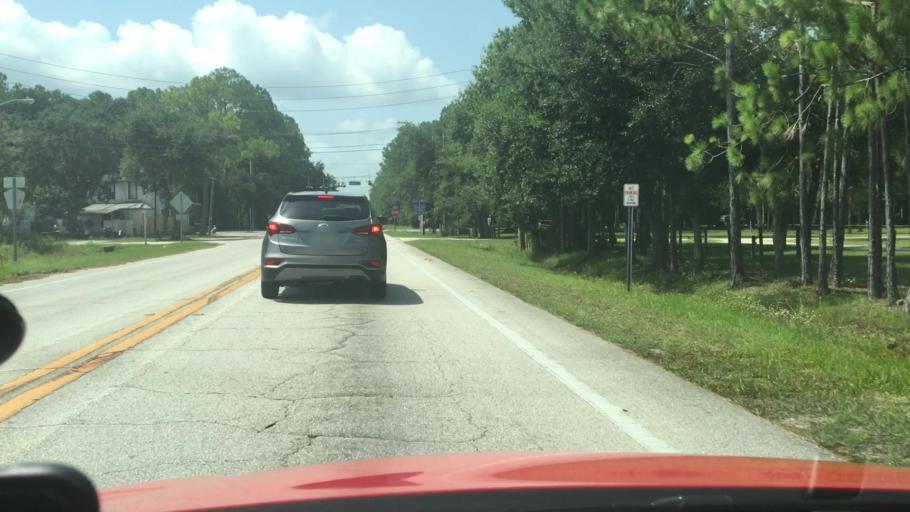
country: US
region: Florida
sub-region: Volusia County
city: Samsula-Spruce Creek
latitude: 29.0447
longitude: -81.0676
